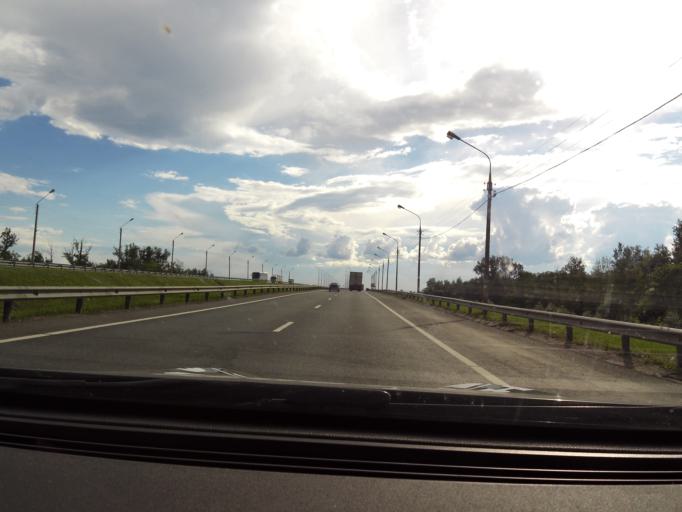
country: RU
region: Vladimir
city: Galitsy
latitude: 56.2252
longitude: 42.7864
